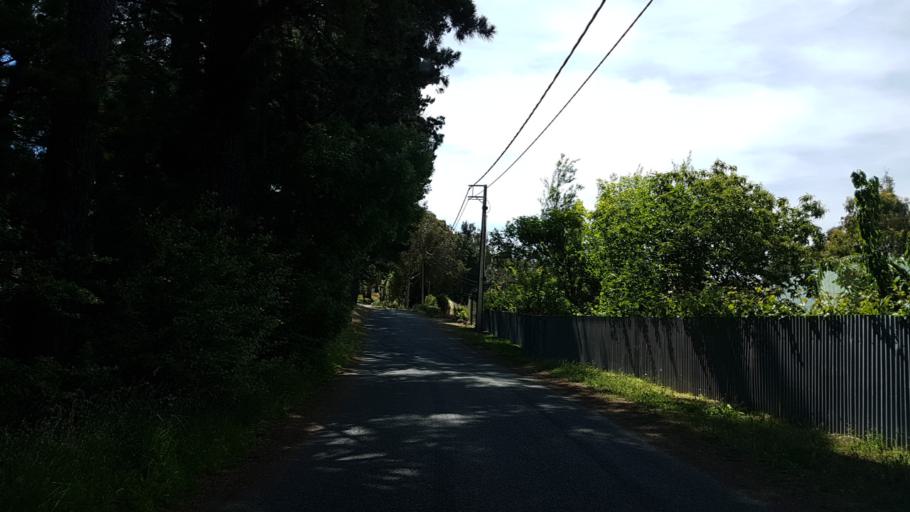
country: AU
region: South Australia
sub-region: Adelaide Hills
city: Adelaide Hills
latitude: -34.9262
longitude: 138.7270
